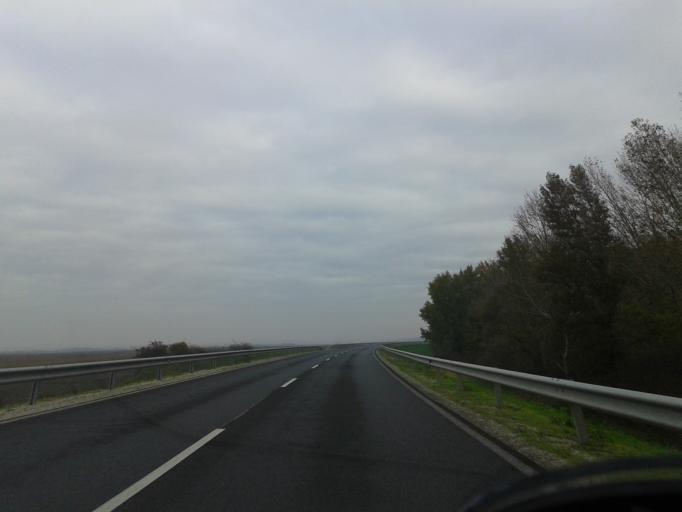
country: HU
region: Fejer
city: Ercsi
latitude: 47.1984
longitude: 18.8727
